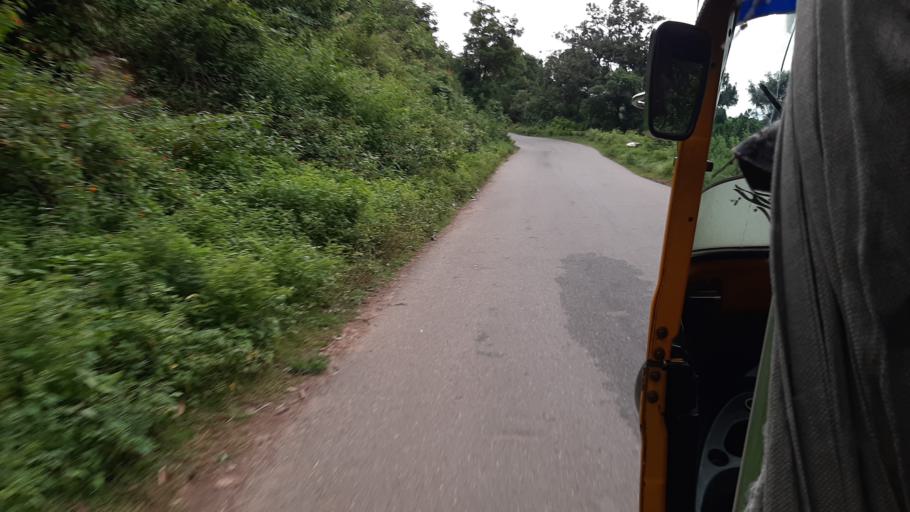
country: IN
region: Andhra Pradesh
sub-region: Vizianagaram District
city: Salur
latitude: 18.2439
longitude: 83.0254
